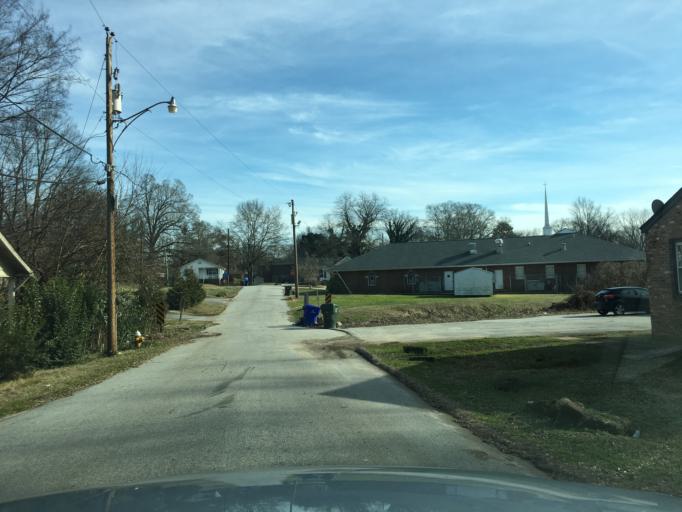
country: US
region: South Carolina
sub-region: Greenville County
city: Greenville
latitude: 34.8564
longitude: -82.4126
